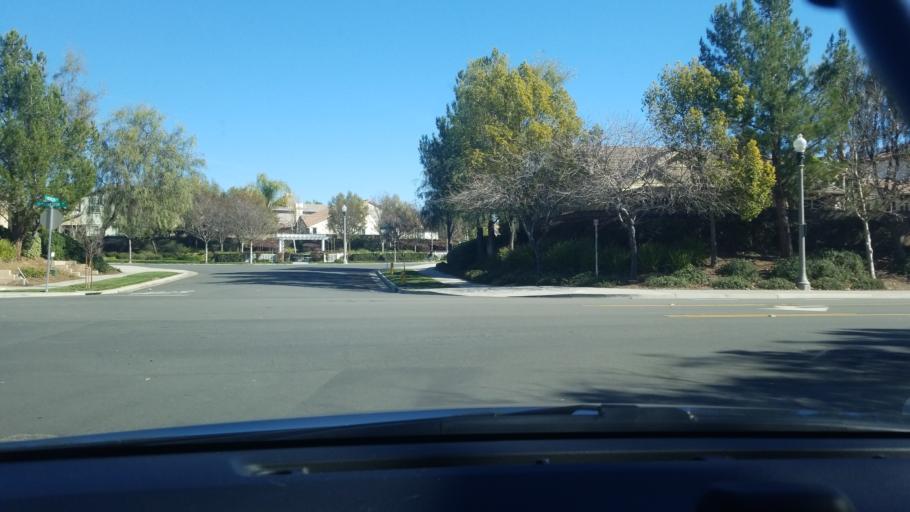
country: US
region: California
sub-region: Riverside County
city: Murrieta Hot Springs
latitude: 33.5358
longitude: -117.1618
